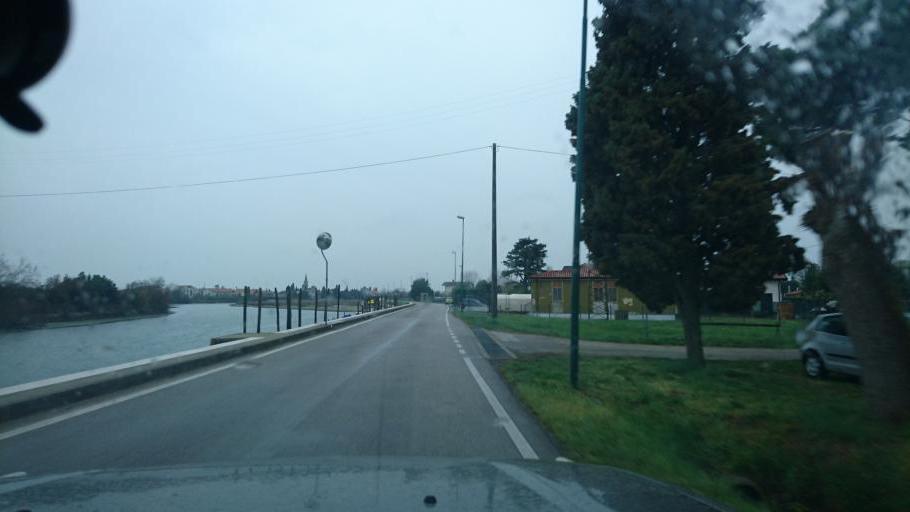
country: IT
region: Veneto
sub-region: Provincia di Venezia
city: Ca' Savio
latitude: 45.4688
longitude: 12.4661
